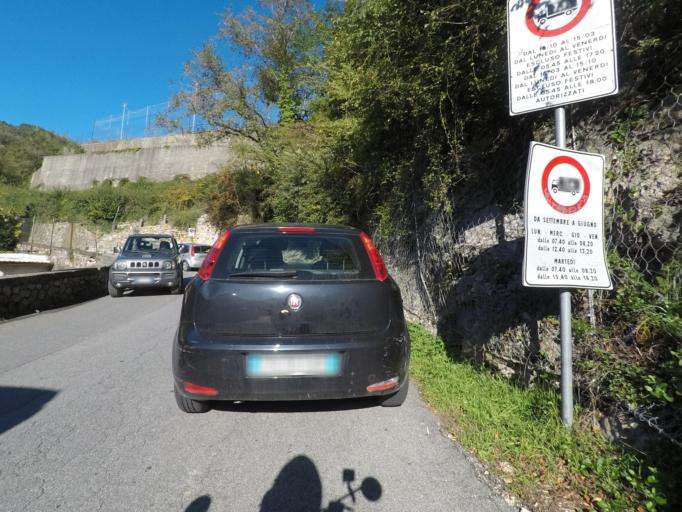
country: IT
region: Tuscany
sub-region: Provincia di Massa-Carrara
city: Carrara
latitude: 44.0976
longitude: 10.0882
